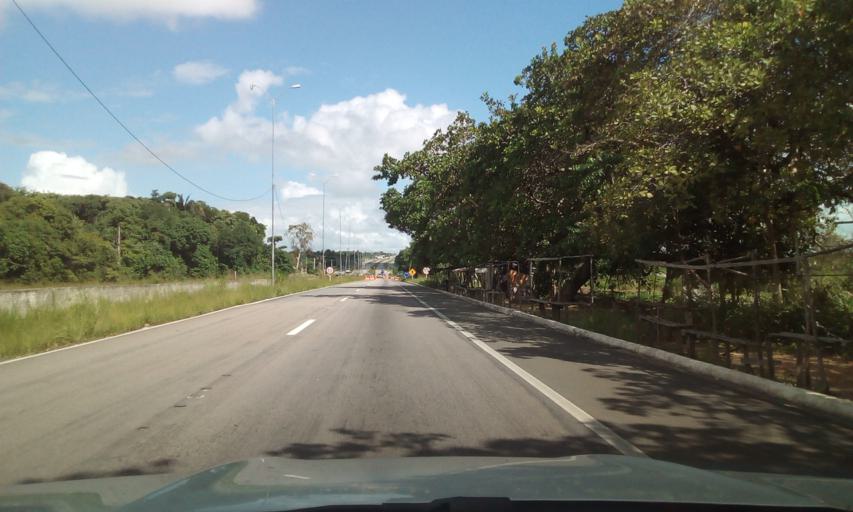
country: BR
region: Paraiba
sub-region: Conde
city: Conde
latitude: -7.3315
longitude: -34.9474
